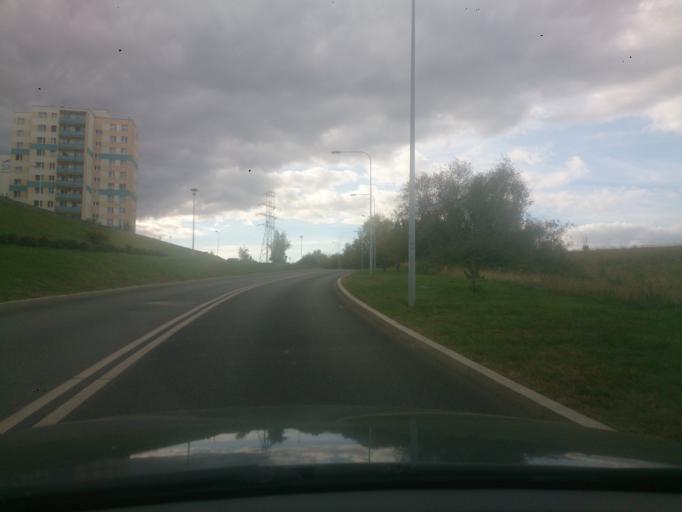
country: PL
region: Kujawsko-Pomorskie
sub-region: Grudziadz
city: Grudziadz
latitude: 53.4681
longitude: 18.7348
